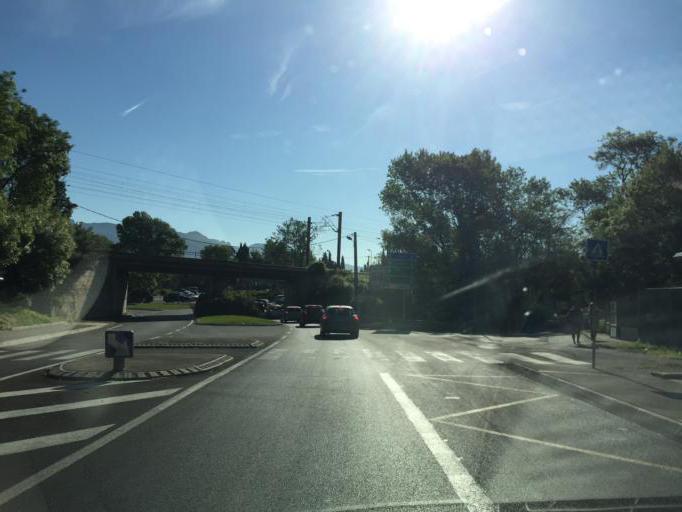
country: FR
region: Provence-Alpes-Cote d'Azur
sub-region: Departement des Bouches-du-Rhone
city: Aubagne
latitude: 43.2962
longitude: 5.5818
